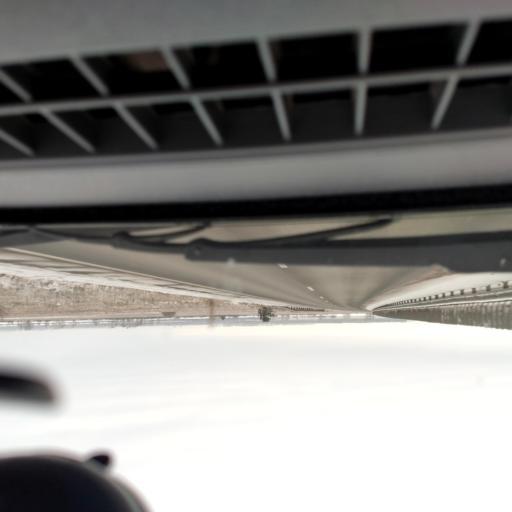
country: RU
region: Bashkortostan
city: Kushnarenkovo
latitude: 55.0664
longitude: 55.3613
